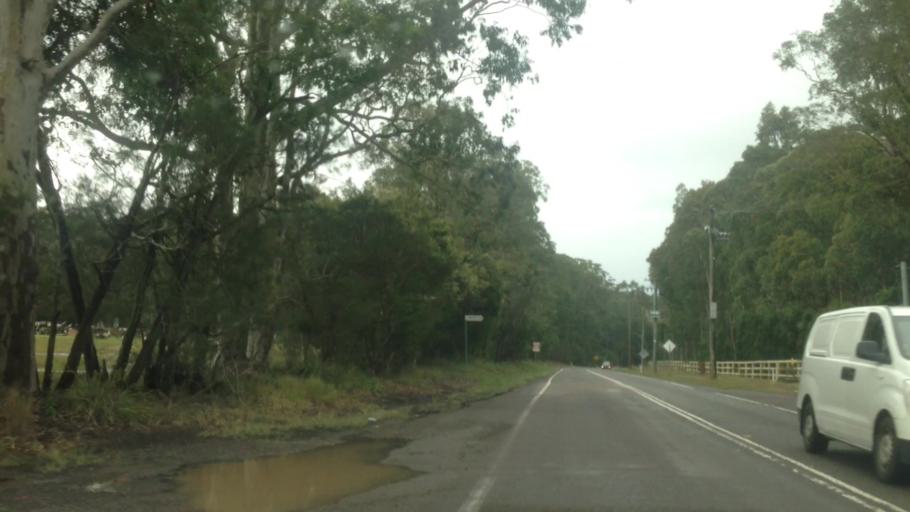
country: AU
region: New South Wales
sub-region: Wyong Shire
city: Little Jilliby
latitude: -33.2617
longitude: 151.3989
